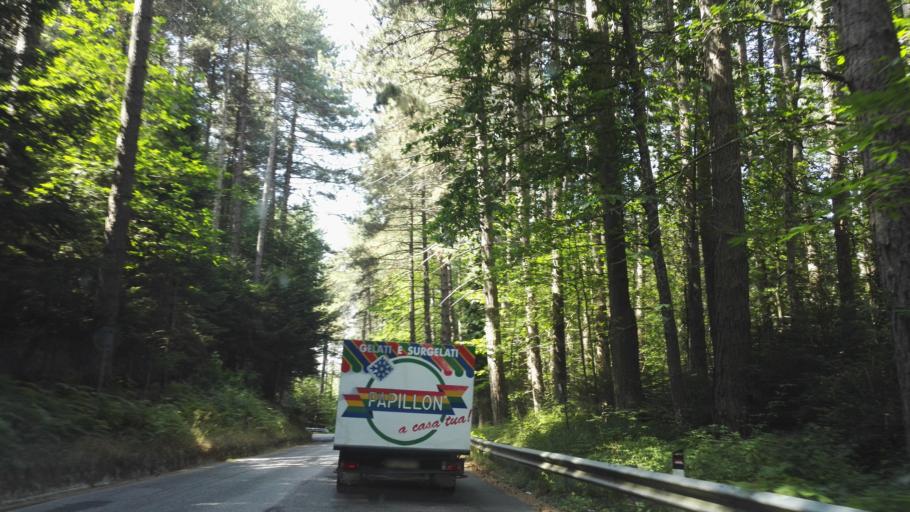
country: IT
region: Calabria
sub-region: Provincia di Vibo-Valentia
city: Mongiana
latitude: 38.5210
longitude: 16.3191
